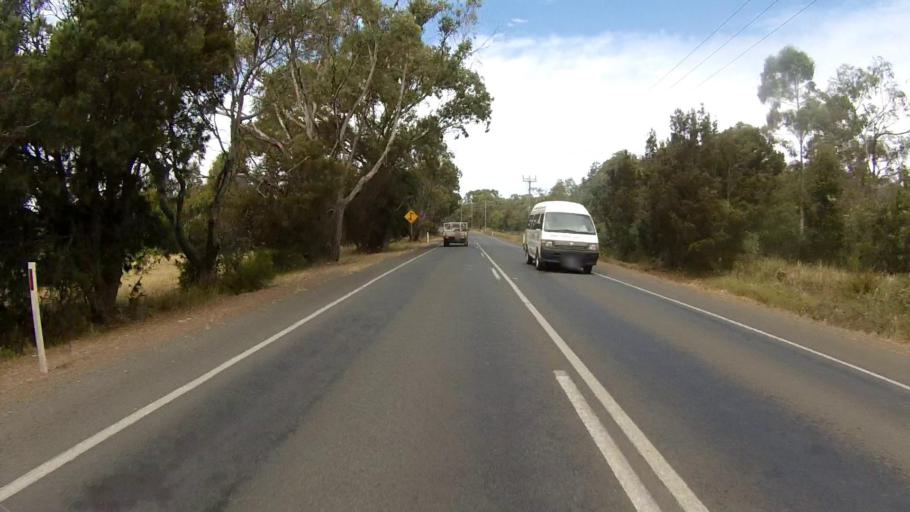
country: AU
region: Tasmania
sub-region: Clarence
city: Sandford
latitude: -42.9418
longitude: 147.4977
